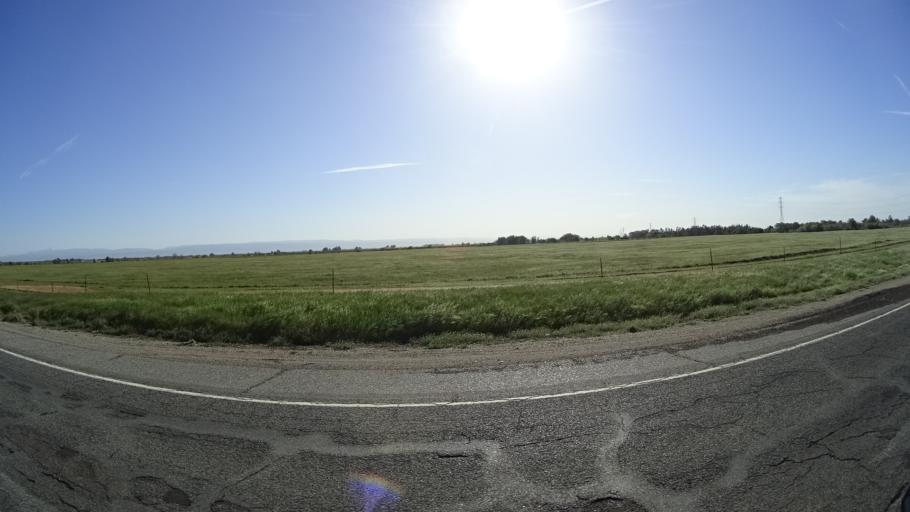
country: US
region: California
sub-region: Glenn County
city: Orland
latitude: 39.8040
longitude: -122.1979
